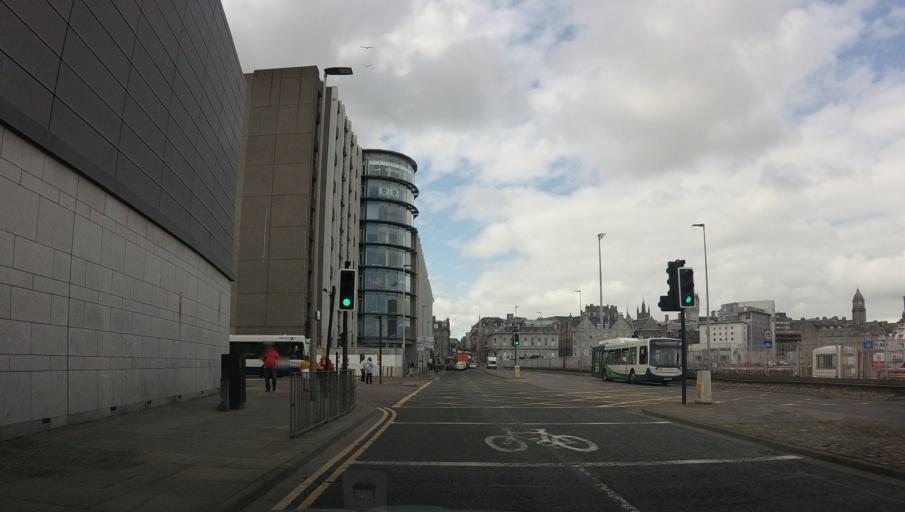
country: GB
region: Scotland
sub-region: Aberdeen City
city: Aberdeen
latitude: 57.1439
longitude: -2.0944
